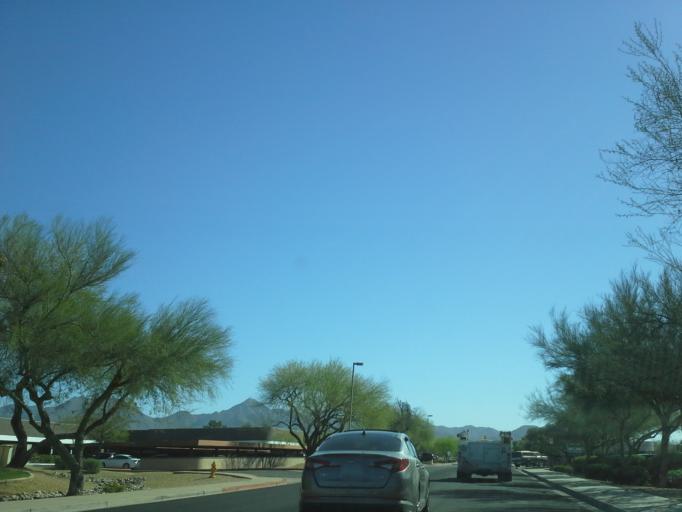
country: US
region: Arizona
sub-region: Maricopa County
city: Paradise Valley
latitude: 33.6166
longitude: -111.9060
